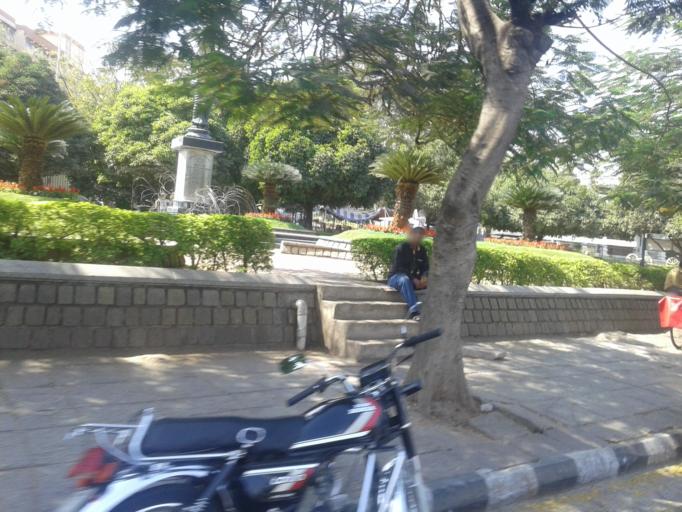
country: IN
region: Telangana
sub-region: Hyderabad
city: Hyderabad
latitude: 17.4093
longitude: 78.4719
